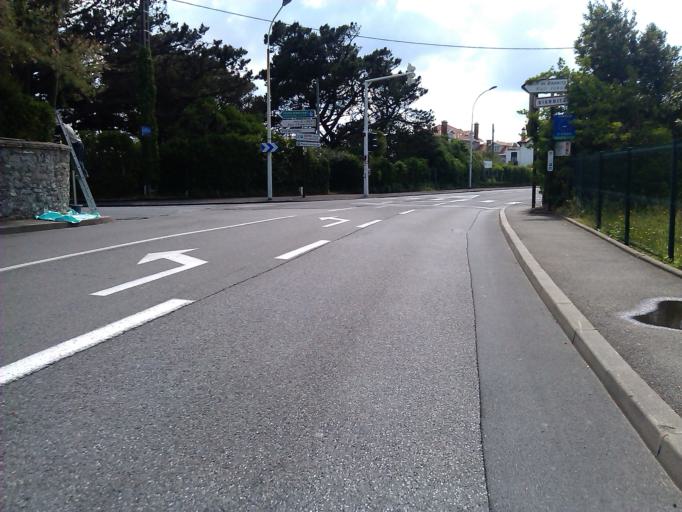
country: FR
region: Aquitaine
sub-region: Departement des Pyrenees-Atlantiques
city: Biarritz
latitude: 43.4927
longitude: -1.5471
